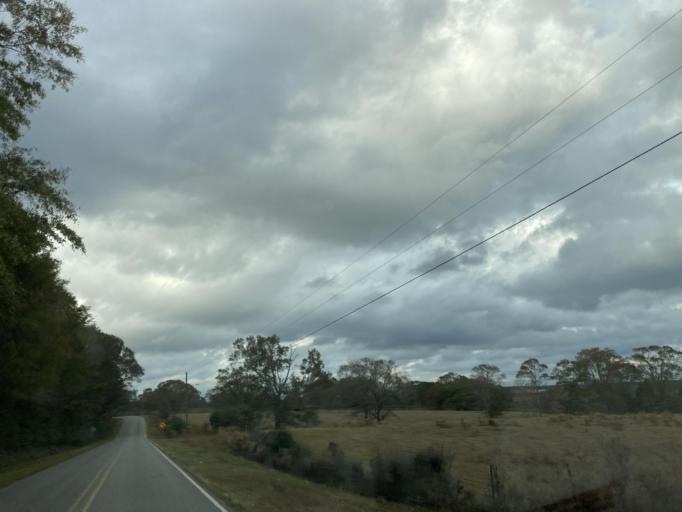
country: US
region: Mississippi
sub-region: Marion County
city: Columbia
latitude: 31.1849
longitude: -89.6641
